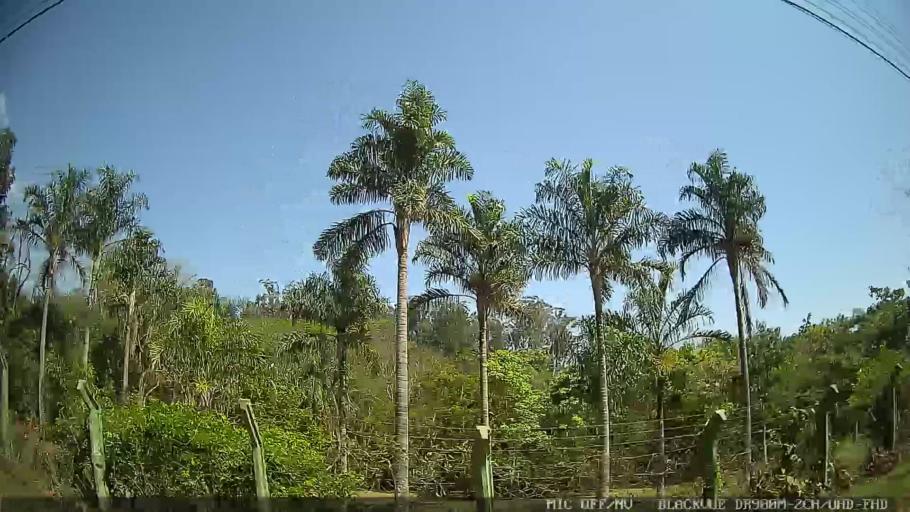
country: BR
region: Sao Paulo
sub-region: Itupeva
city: Itupeva
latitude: -23.2140
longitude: -47.0795
